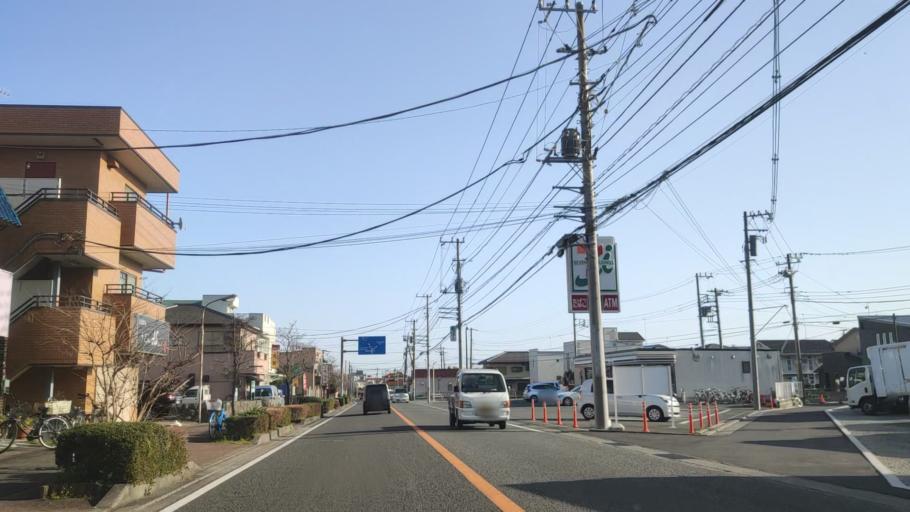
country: JP
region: Kanagawa
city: Zama
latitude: 35.5077
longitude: 139.3397
